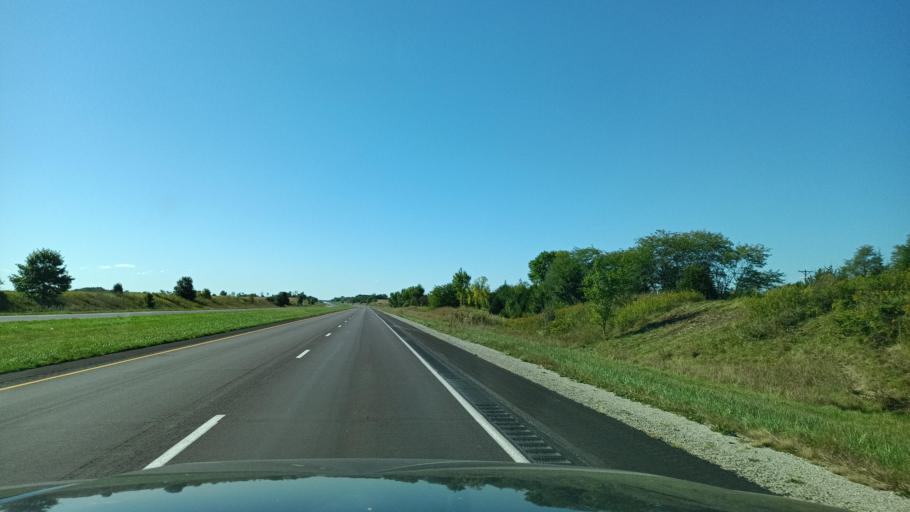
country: US
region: Illinois
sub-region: Hancock County
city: Nauvoo
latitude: 40.4998
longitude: -91.4434
